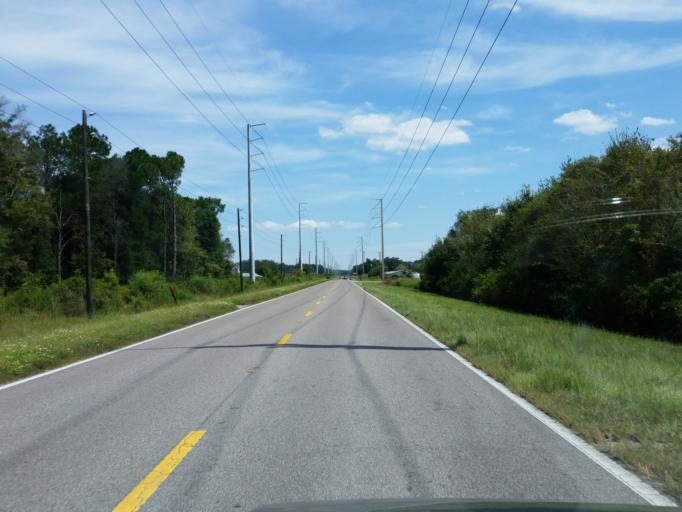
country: US
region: Florida
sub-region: Pasco County
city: Zephyrhills North
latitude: 28.2593
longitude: -82.0987
